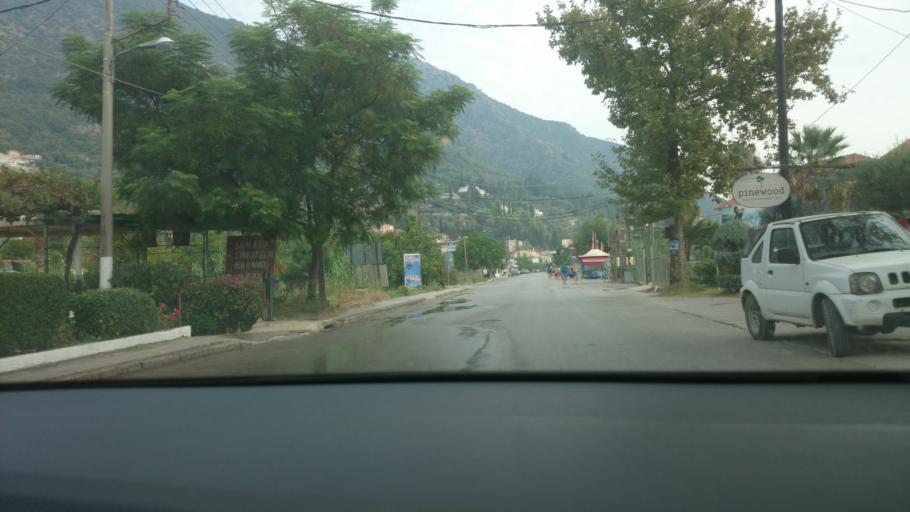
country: GR
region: Ionian Islands
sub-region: Lefkada
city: Nidri
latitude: 38.7132
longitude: 20.7149
